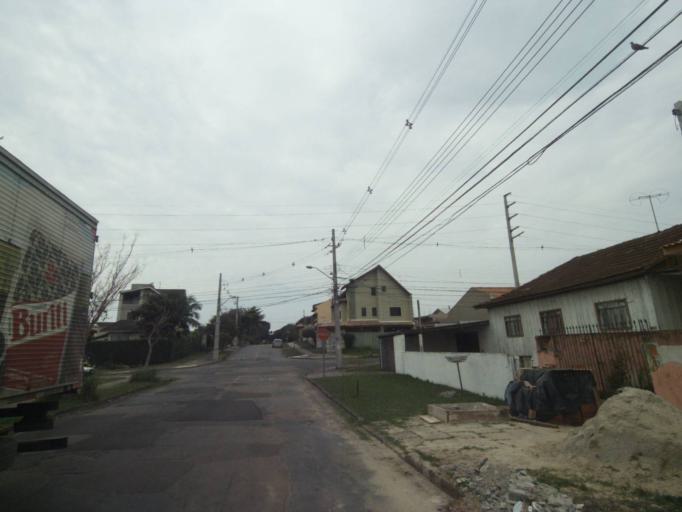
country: BR
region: Parana
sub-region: Curitiba
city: Curitiba
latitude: -25.4630
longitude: -49.3025
